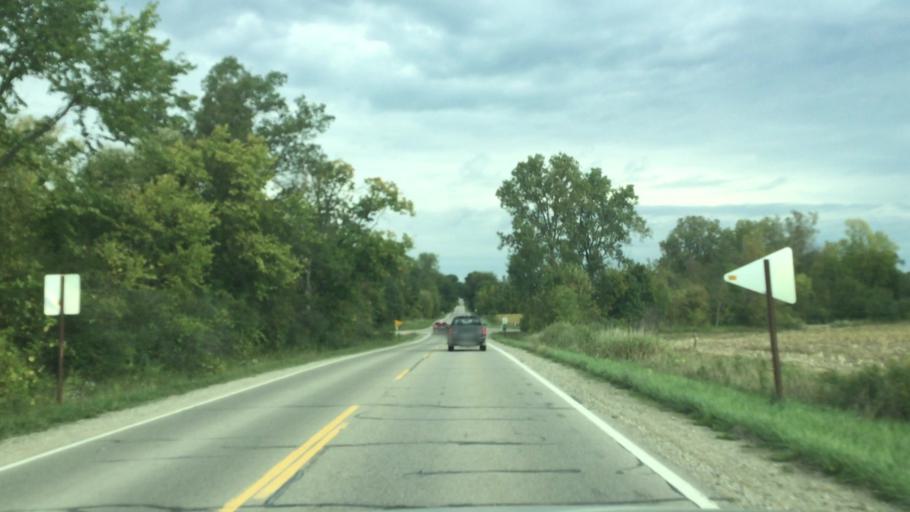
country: US
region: Michigan
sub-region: Livingston County
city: Howell
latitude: 42.6433
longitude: -83.8759
